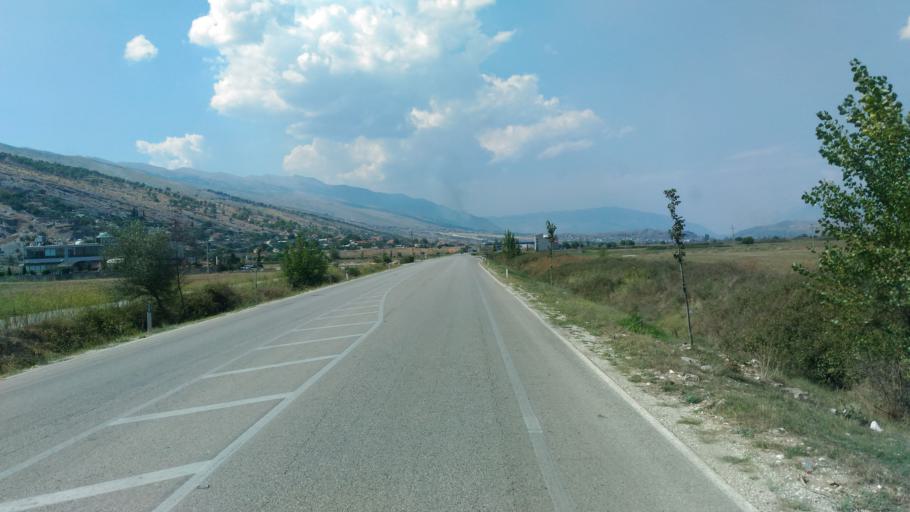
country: AL
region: Gjirokaster
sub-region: Rrethi i Gjirokastres
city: Dervician
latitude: 40.0118
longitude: 20.2021
